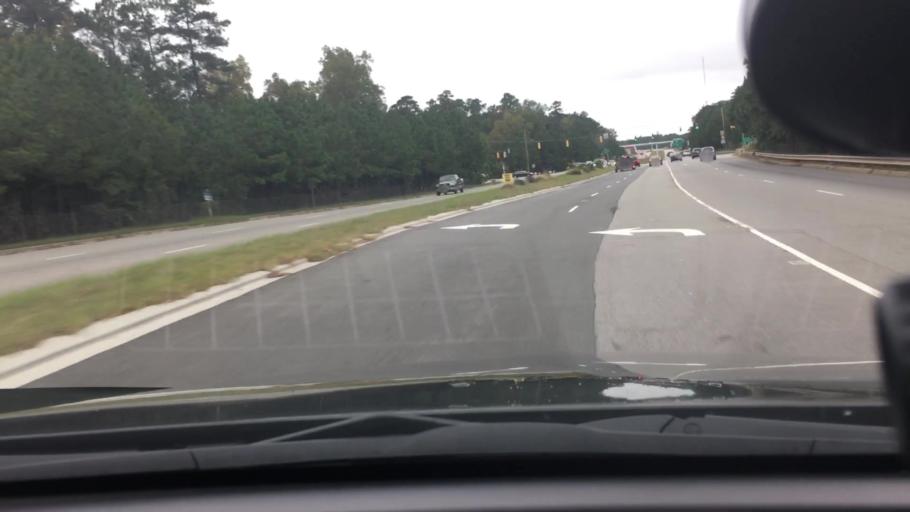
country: US
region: North Carolina
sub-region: Wake County
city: Apex
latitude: 35.6960
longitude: -78.8342
